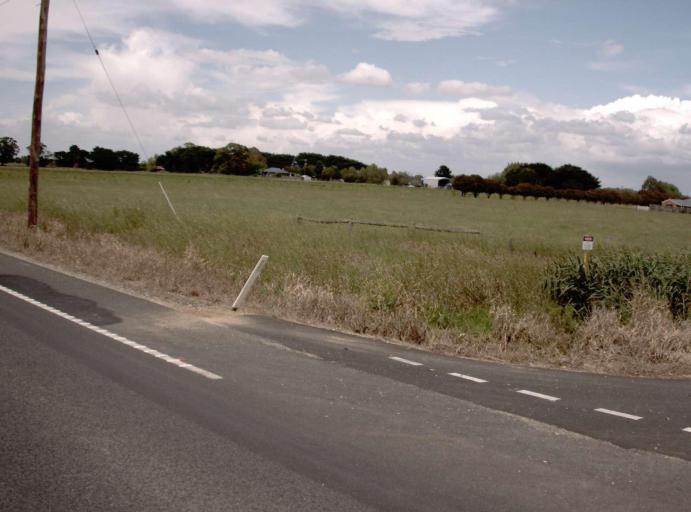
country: AU
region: Victoria
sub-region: Wellington
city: Sale
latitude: -38.0543
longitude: 147.0248
